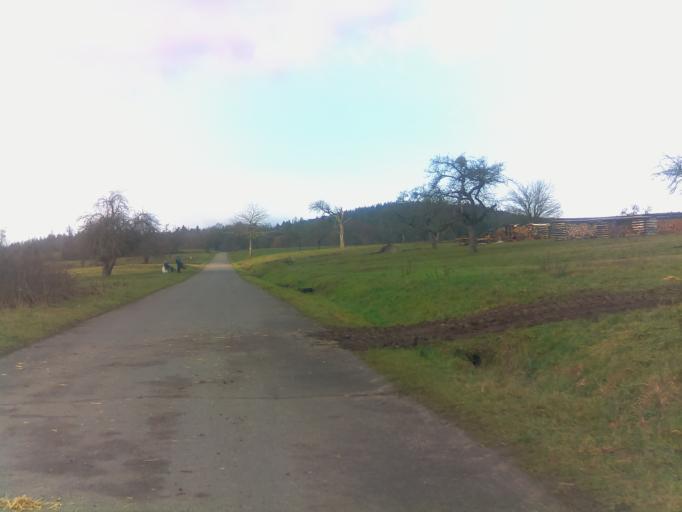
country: DE
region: Bavaria
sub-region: Regierungsbezirk Unterfranken
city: Neunkirchen
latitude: 49.8000
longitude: 9.4078
